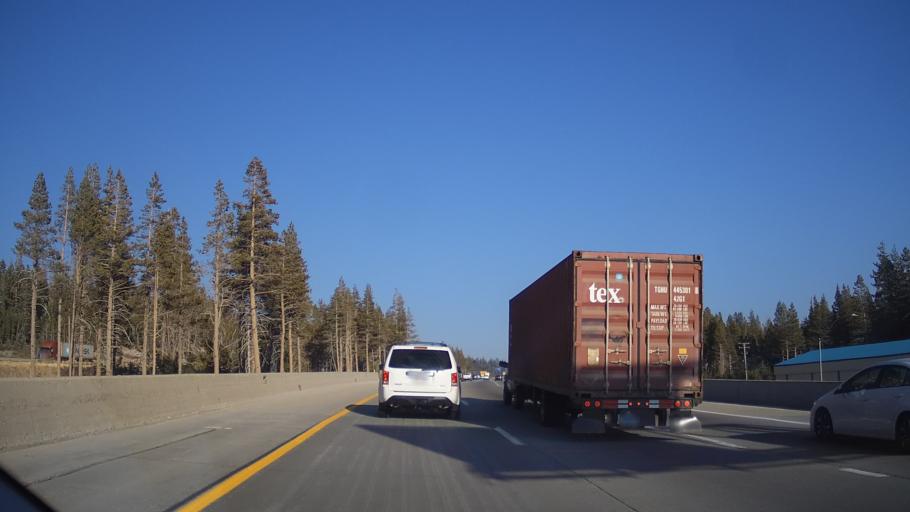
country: US
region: California
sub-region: Nevada County
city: Truckee
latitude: 39.3386
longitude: -120.3501
